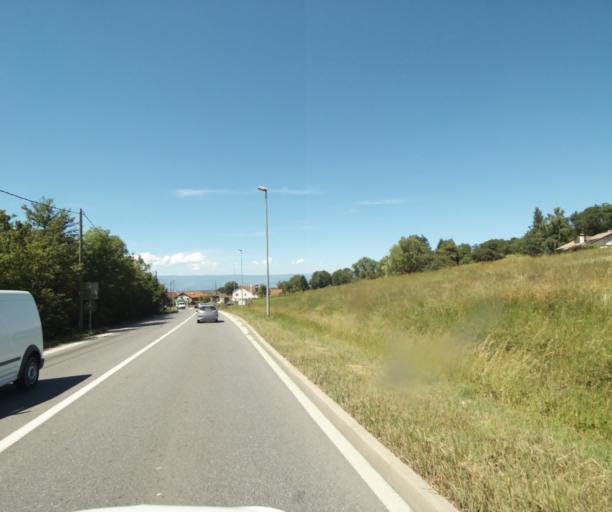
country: FR
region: Rhone-Alpes
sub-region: Departement de la Haute-Savoie
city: Loisin
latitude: 46.2694
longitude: 6.3139
